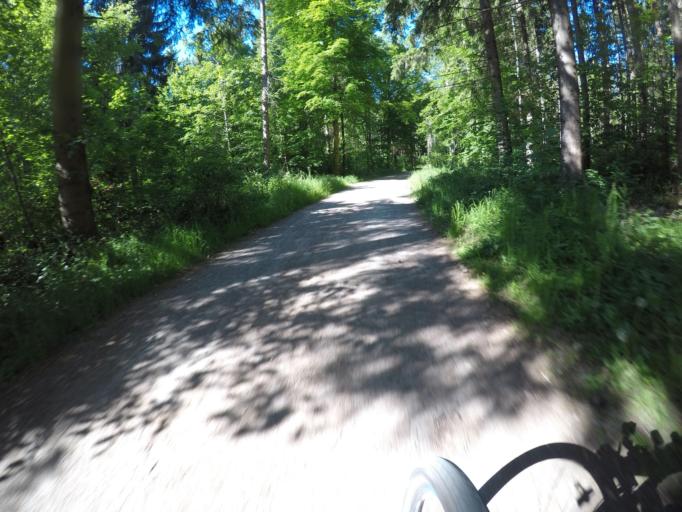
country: DE
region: Baden-Wuerttemberg
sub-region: Regierungsbezirk Stuttgart
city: Gerlingen
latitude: 48.7451
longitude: 9.0771
